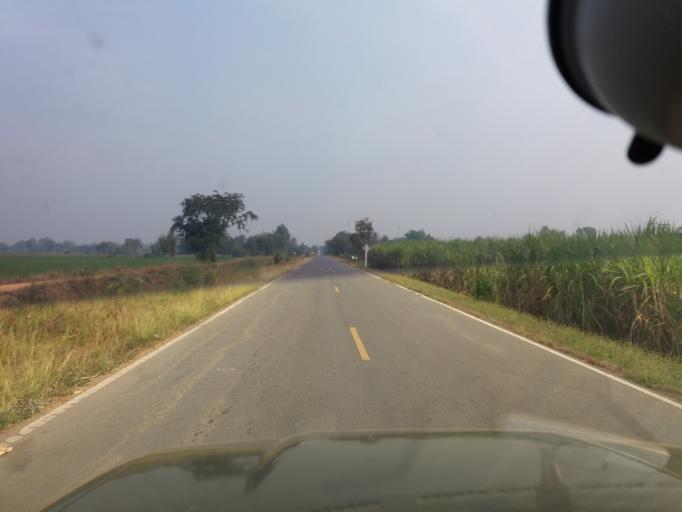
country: TH
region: Suphan Buri
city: Doem Bang Nang Buat
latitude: 14.8662
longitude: 100.1697
